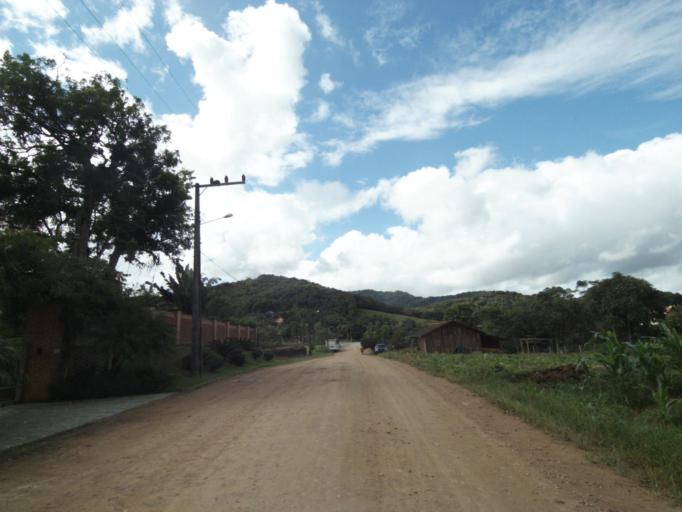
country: BR
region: Santa Catarina
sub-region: Pomerode
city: Pomerode
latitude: -26.6740
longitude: -49.1867
